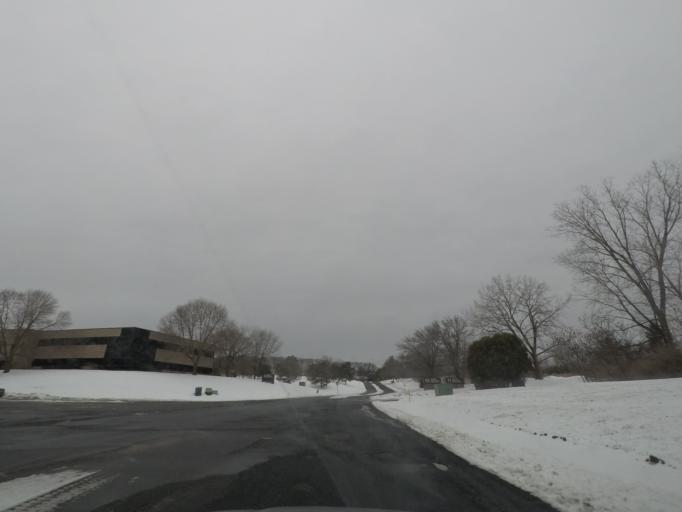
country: US
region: New York
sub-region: Schenectady County
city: Niskayuna
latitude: 42.7591
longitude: -73.8175
